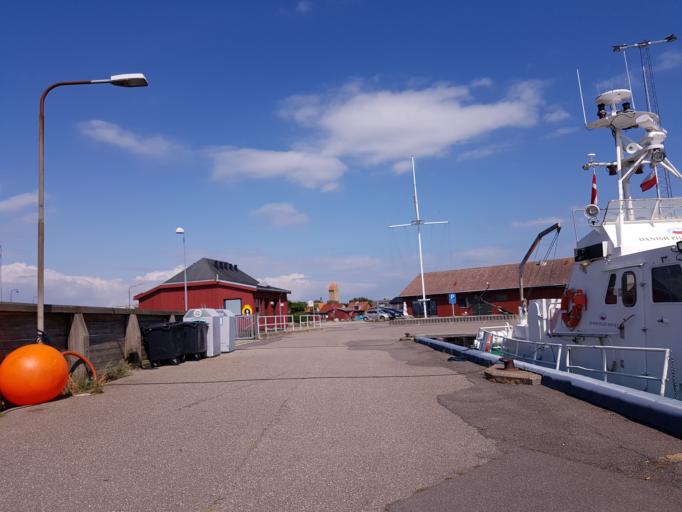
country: DK
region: Zealand
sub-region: Guldborgsund Kommune
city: Nykobing Falster
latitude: 54.5725
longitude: 11.9290
